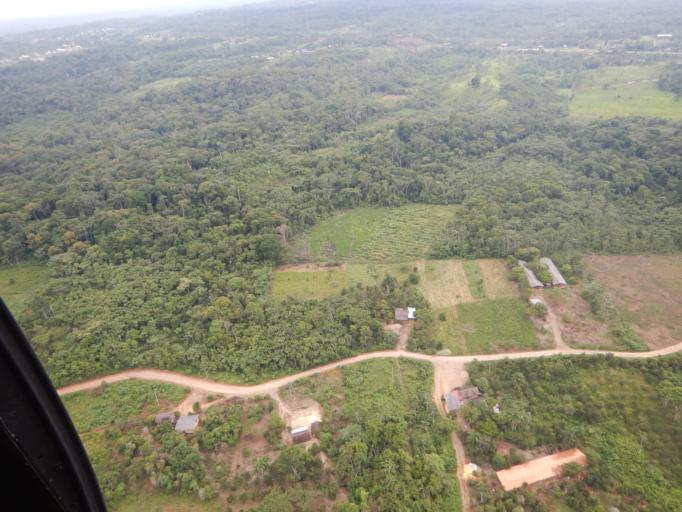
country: BO
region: Cochabamba
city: Chimore
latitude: -17.0910
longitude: -64.8421
